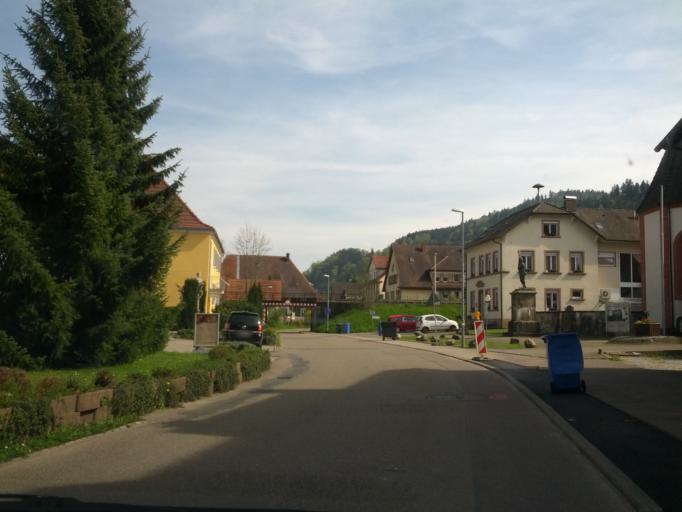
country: DE
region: Baden-Wuerttemberg
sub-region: Freiburg Region
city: Gutach im Breisgau
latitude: 48.1253
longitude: 8.0050
